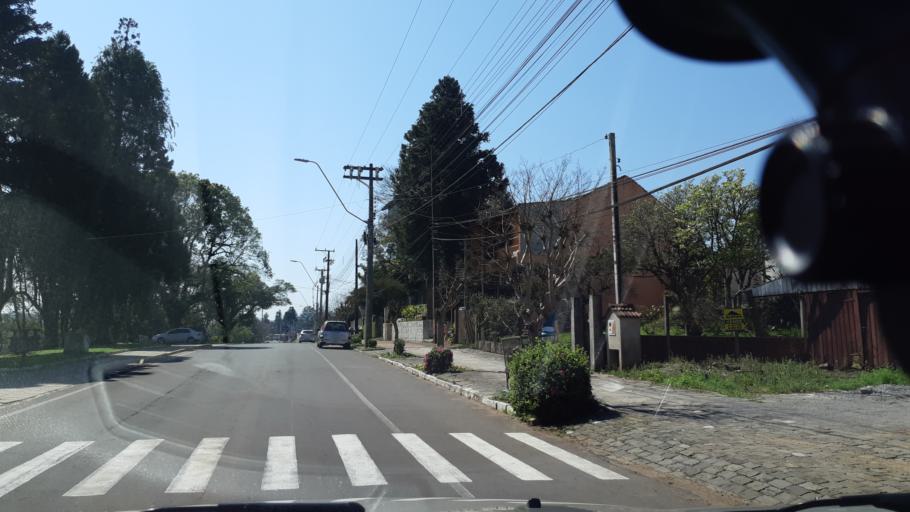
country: BR
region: Rio Grande do Sul
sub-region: Nova Petropolis
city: Nova Petropolis
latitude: -29.3843
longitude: -51.1204
